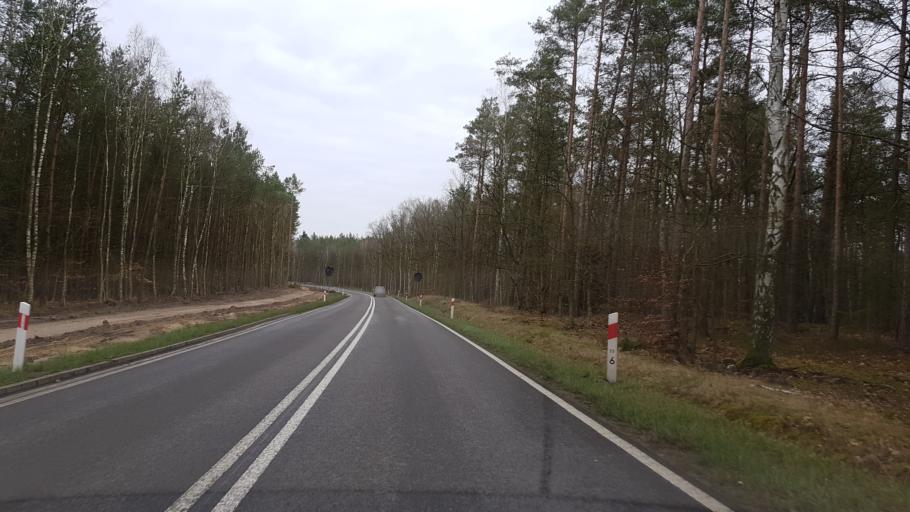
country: PL
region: West Pomeranian Voivodeship
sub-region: Powiat policki
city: Police
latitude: 53.6375
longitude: 14.5056
